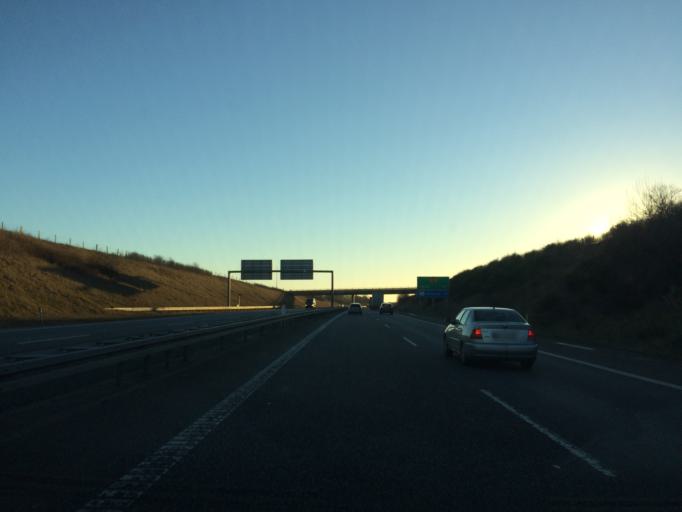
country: DK
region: Central Jutland
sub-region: Herning Kommune
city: Lind
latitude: 56.1026
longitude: 9.0075
